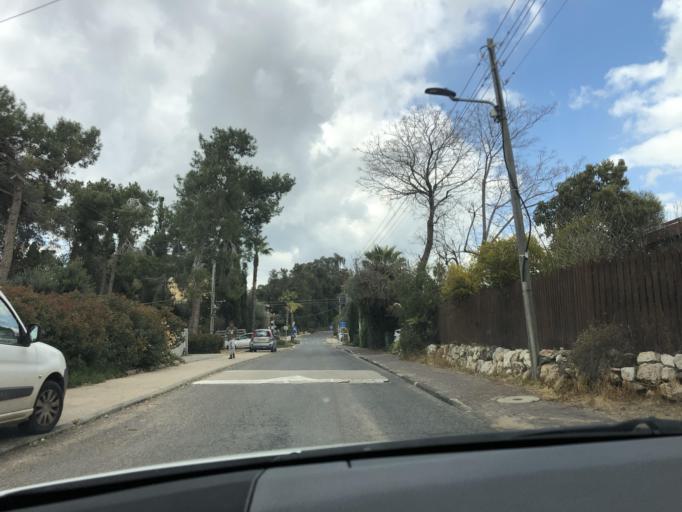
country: IL
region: Central District
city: Tel Mond
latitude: 32.2636
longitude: 34.9319
